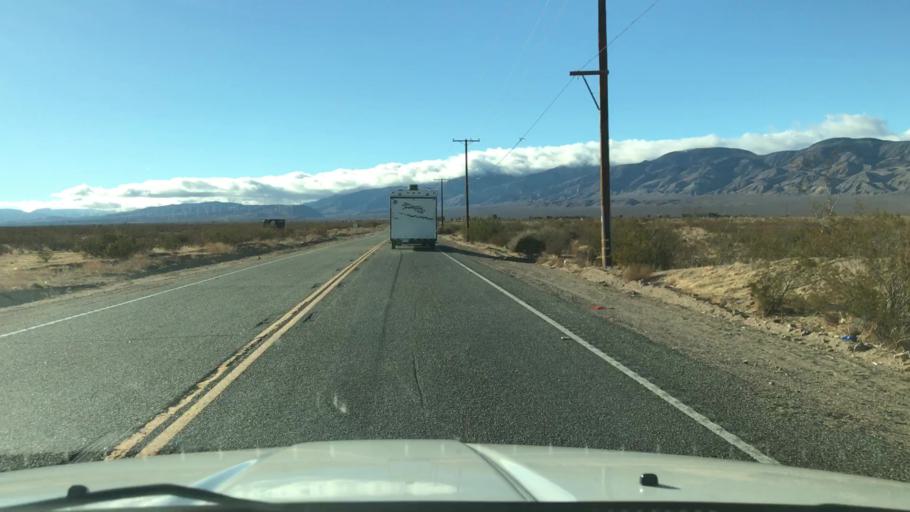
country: US
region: California
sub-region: Kern County
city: California City
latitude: 35.1256
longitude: -118.0910
